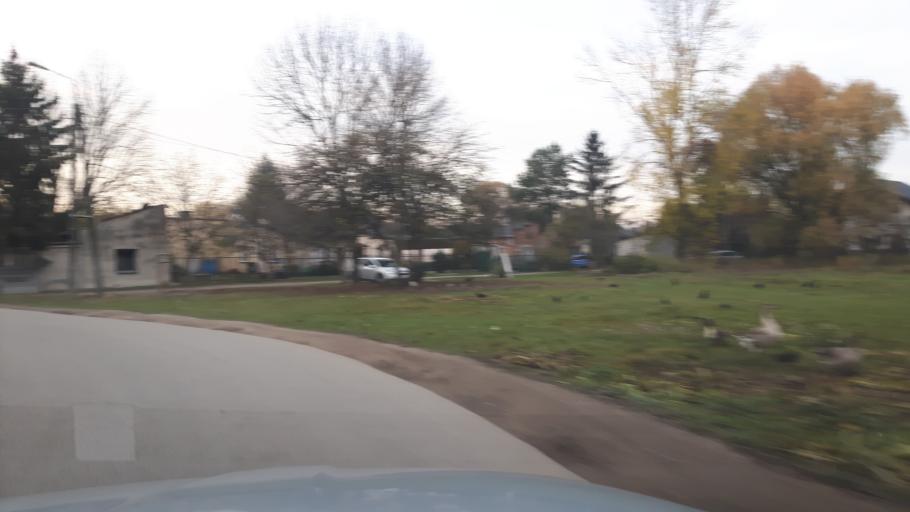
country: PL
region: Masovian Voivodeship
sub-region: Warszawa
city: Wilanow
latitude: 52.1885
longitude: 21.0976
